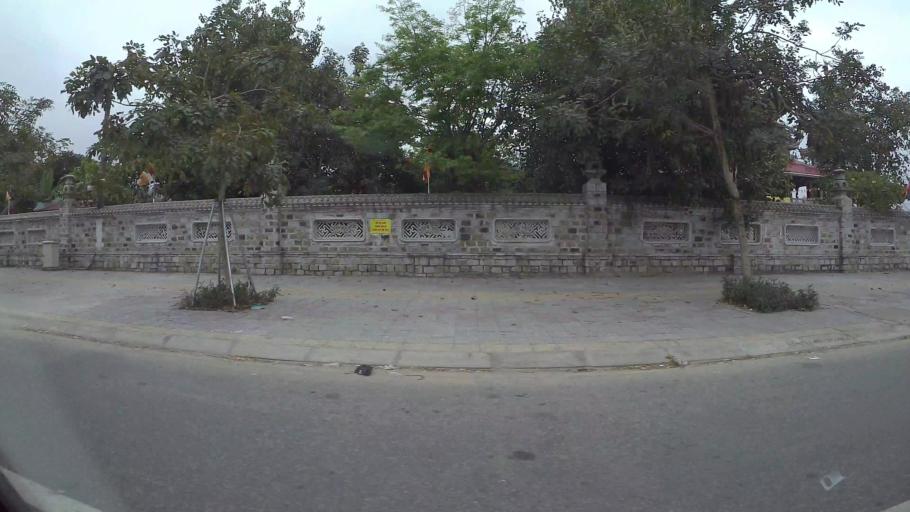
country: VN
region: Da Nang
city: Lien Chieu
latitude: 16.0655
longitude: 108.1732
